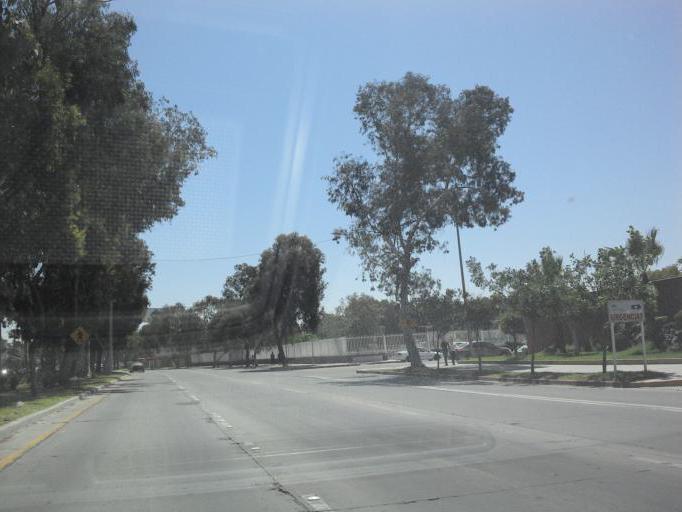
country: MX
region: Baja California
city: Tijuana
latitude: 32.5188
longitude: -117.0074
